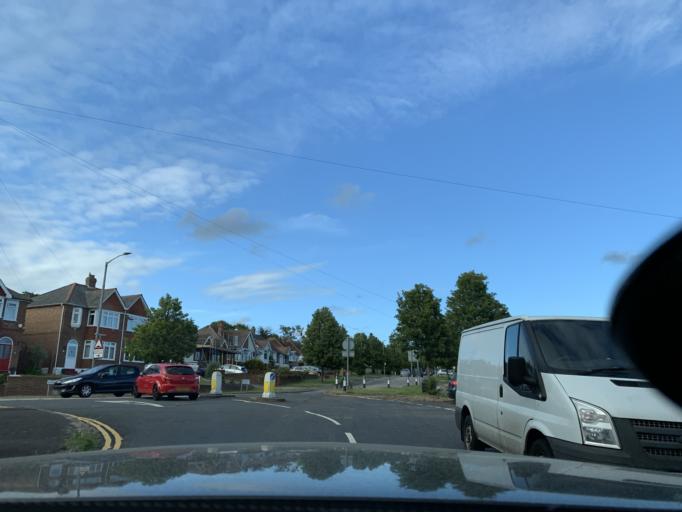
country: GB
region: England
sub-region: East Sussex
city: Saint Leonards-on-Sea
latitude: 50.8754
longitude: 0.5542
